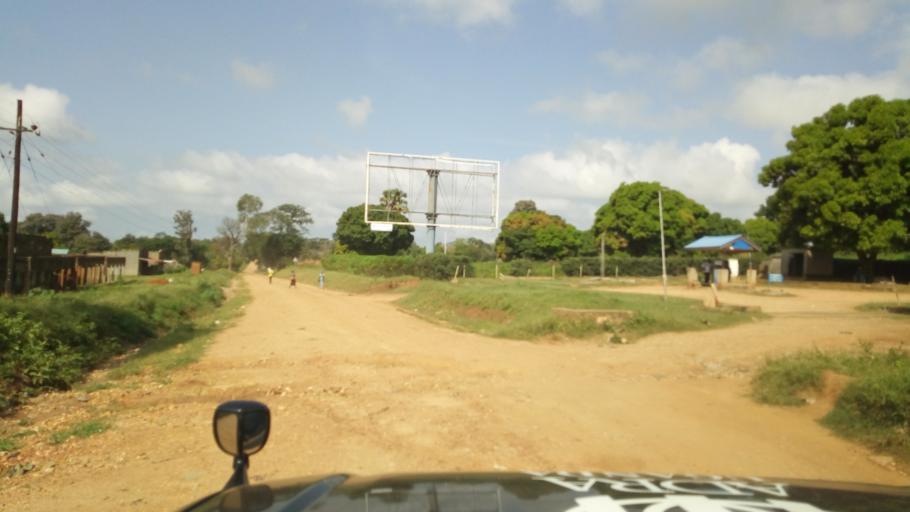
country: UG
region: Northern Region
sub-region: Moyo District
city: Moyo
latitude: 3.6548
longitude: 31.7189
